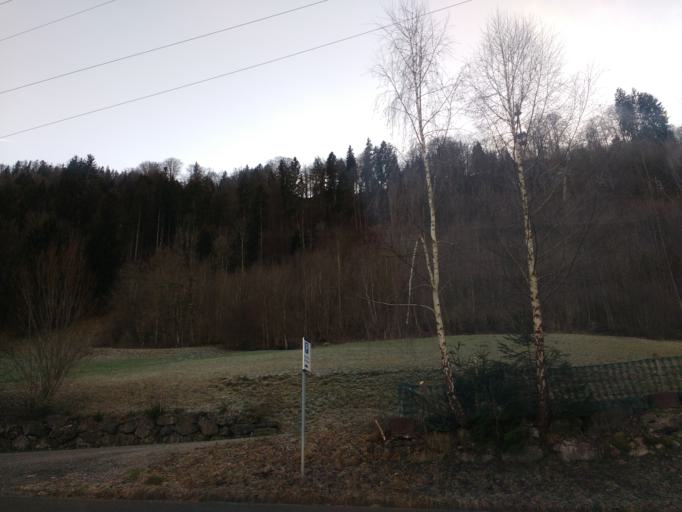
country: DE
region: Bavaria
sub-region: Swabia
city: Immenstadt im Allgau
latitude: 47.5541
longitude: 10.2197
